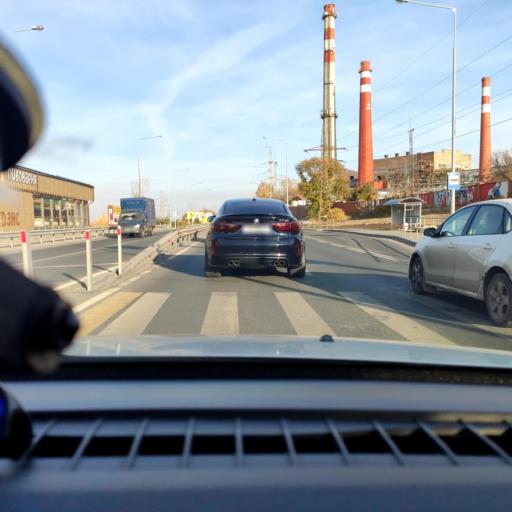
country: RU
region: Samara
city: Volzhskiy
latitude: 53.3778
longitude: 50.1714
